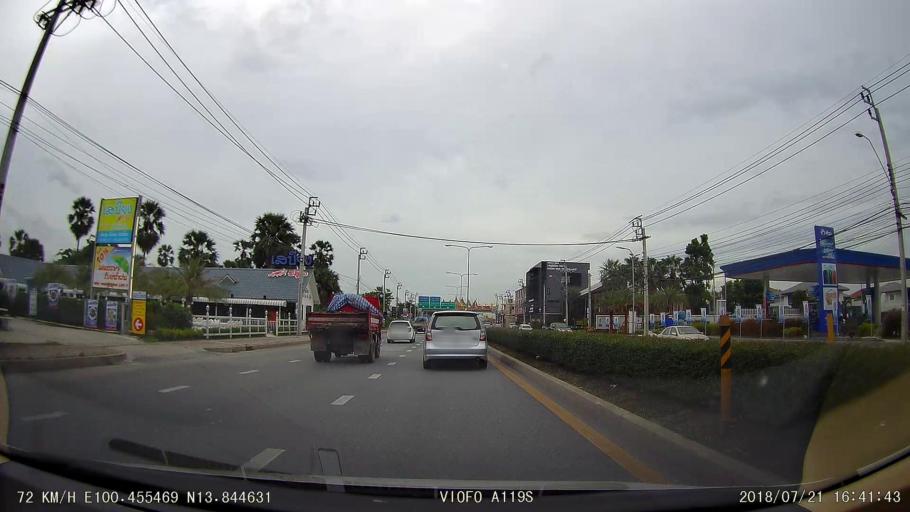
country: TH
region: Nonthaburi
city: Bang Kruai
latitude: 13.8447
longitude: 100.4552
